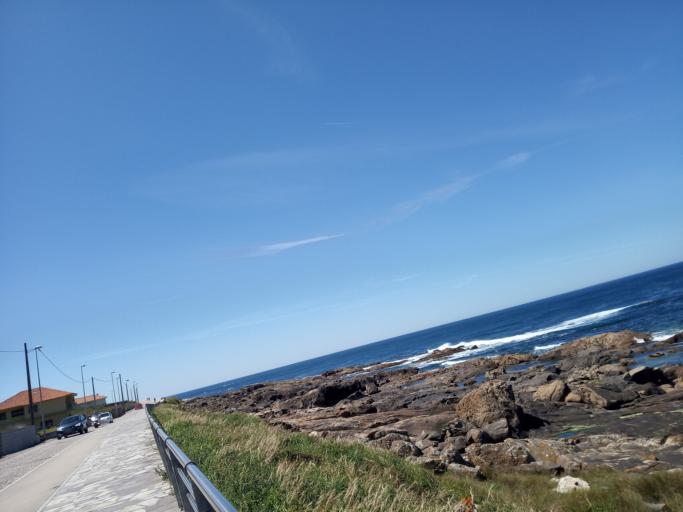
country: ES
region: Galicia
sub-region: Provincia de Pontevedra
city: A Guarda
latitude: 41.8937
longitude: -8.8794
